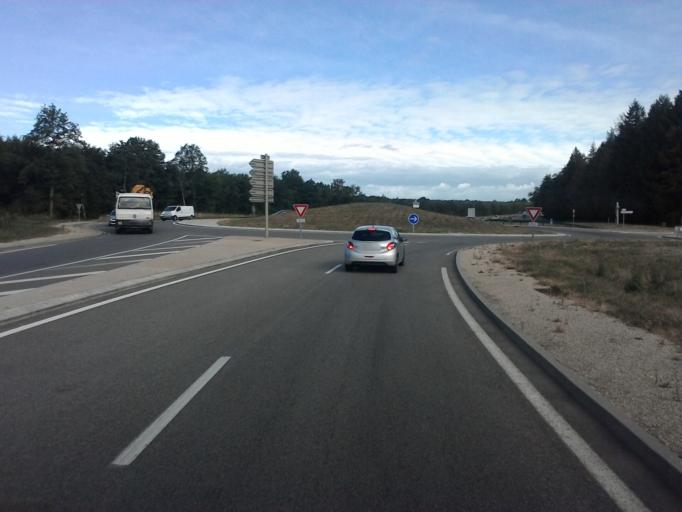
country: FR
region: Rhone-Alpes
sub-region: Departement de l'Ain
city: Montagnat
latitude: 46.1654
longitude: 5.2654
